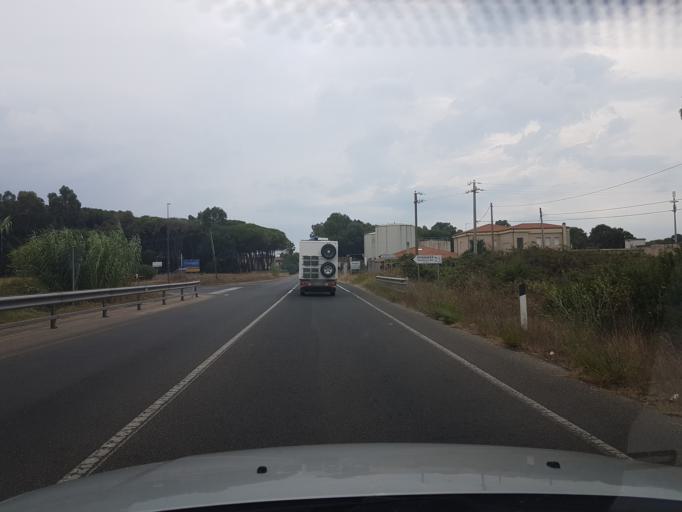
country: IT
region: Sardinia
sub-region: Provincia di Oristano
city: Cabras
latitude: 39.9086
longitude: 8.5225
